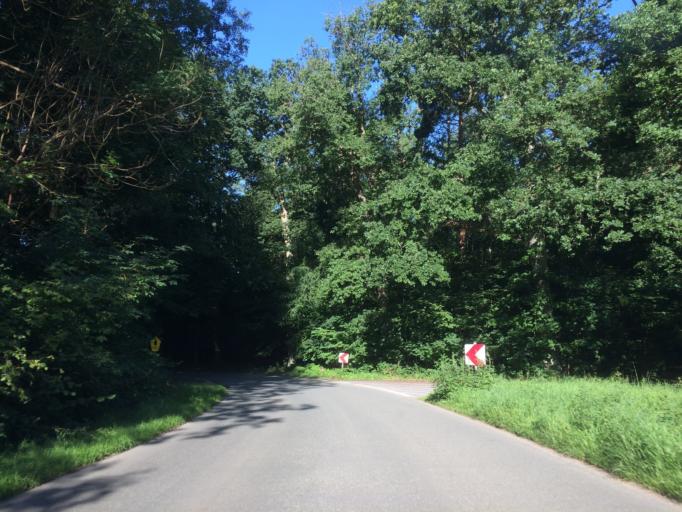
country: DE
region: Schleswig-Holstein
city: Bosdorf
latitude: 54.1573
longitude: 10.4764
